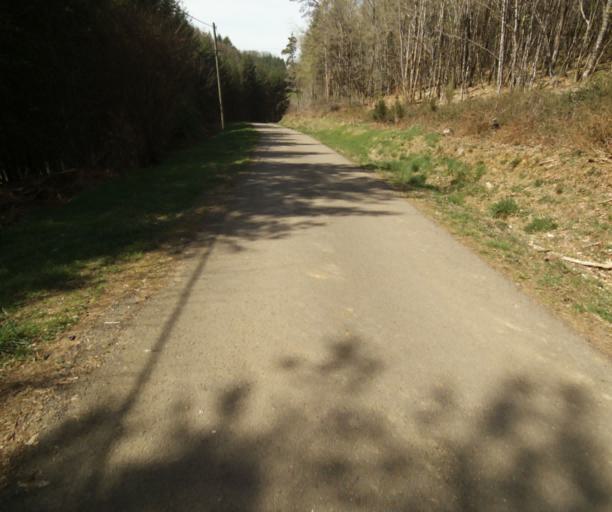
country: FR
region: Limousin
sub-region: Departement de la Correze
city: Seilhac
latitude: 45.3996
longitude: 1.7721
